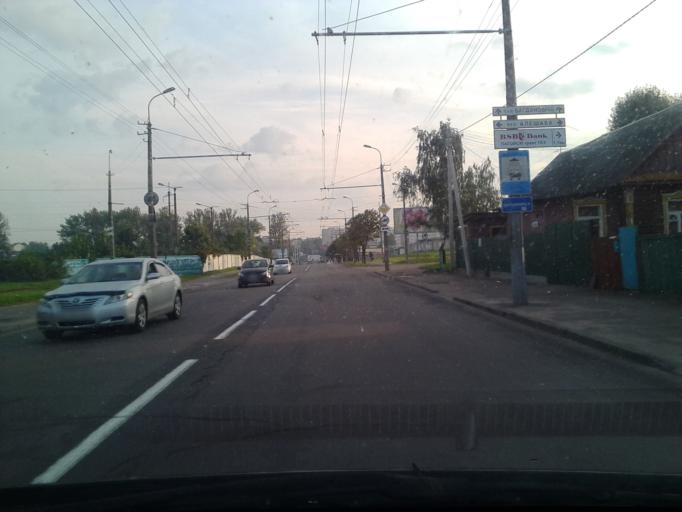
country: BY
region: Minsk
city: Minsk
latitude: 53.9470
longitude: 27.5941
